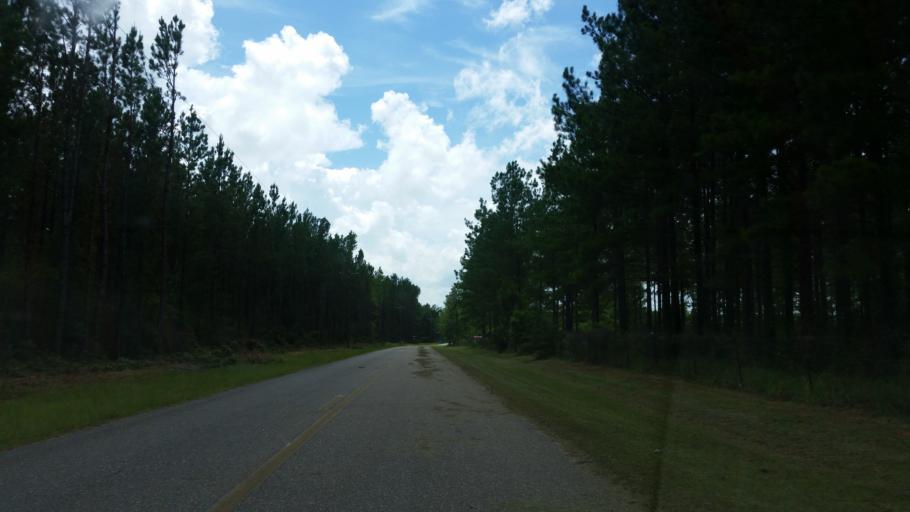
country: US
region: Florida
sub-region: Santa Rosa County
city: Point Baker
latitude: 30.7369
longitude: -86.8524
